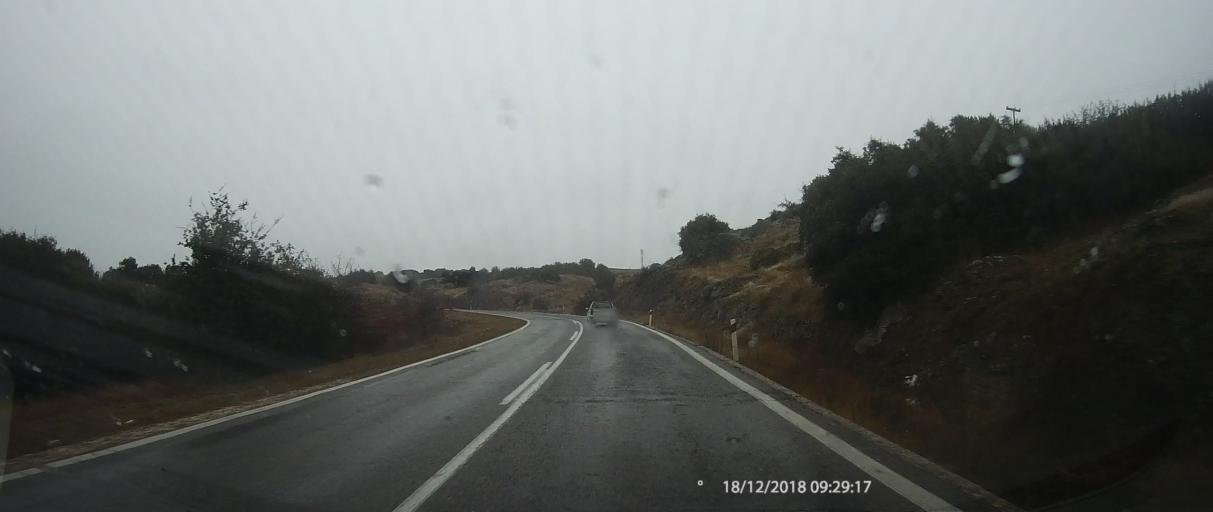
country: GR
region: Thessaly
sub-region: Nomos Larisis
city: Elassona
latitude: 39.9268
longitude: 22.1713
